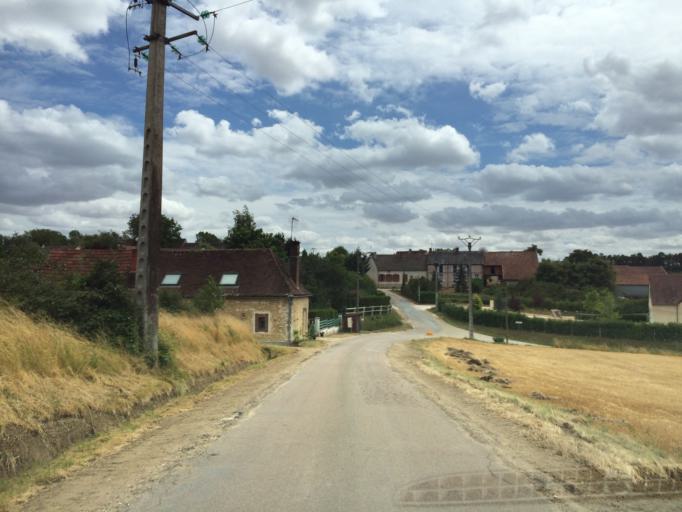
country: FR
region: Bourgogne
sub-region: Departement de l'Yonne
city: Fleury-la-Vallee
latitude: 47.8486
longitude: 3.4043
